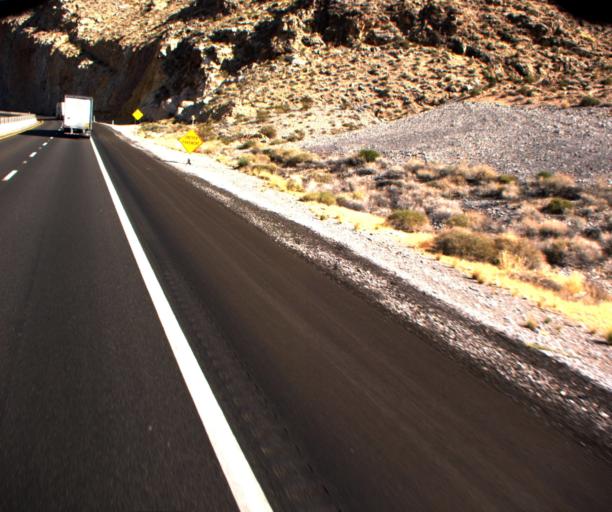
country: US
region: Arizona
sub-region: Mohave County
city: Beaver Dam
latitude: 36.9180
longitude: -113.8663
